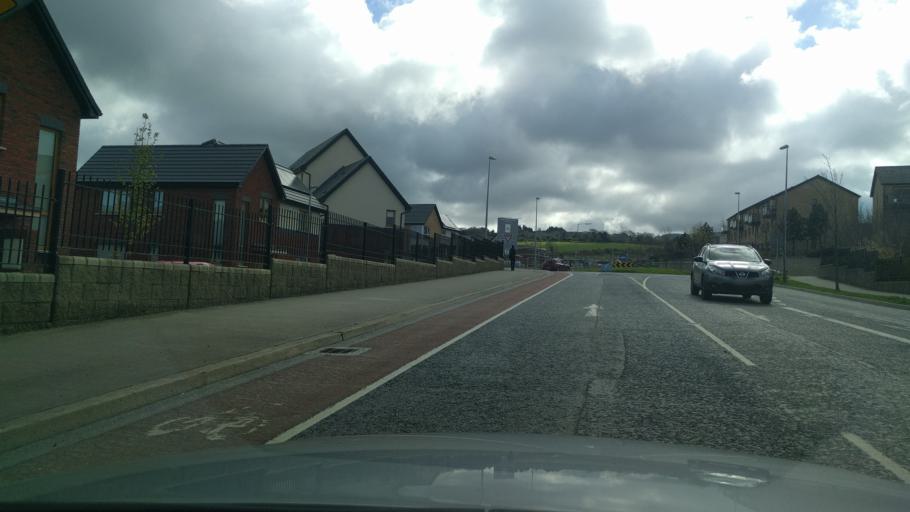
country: IE
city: Knocklyon
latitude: 53.2713
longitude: -6.3284
